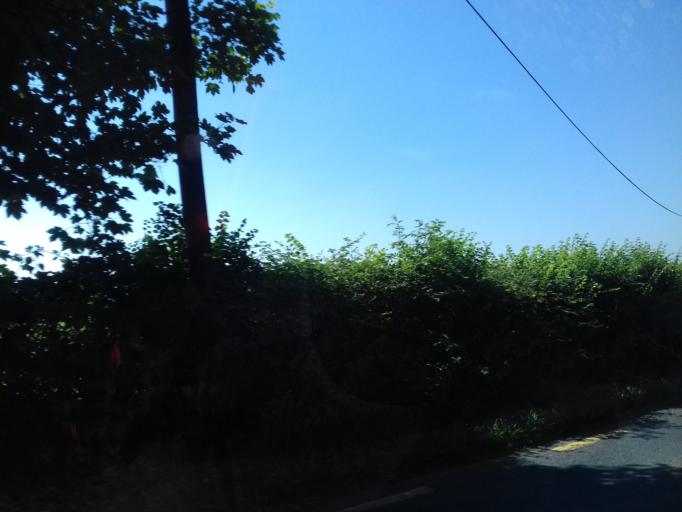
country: IE
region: Leinster
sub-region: Fingal County
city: Swords
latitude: 53.4735
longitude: -6.2727
